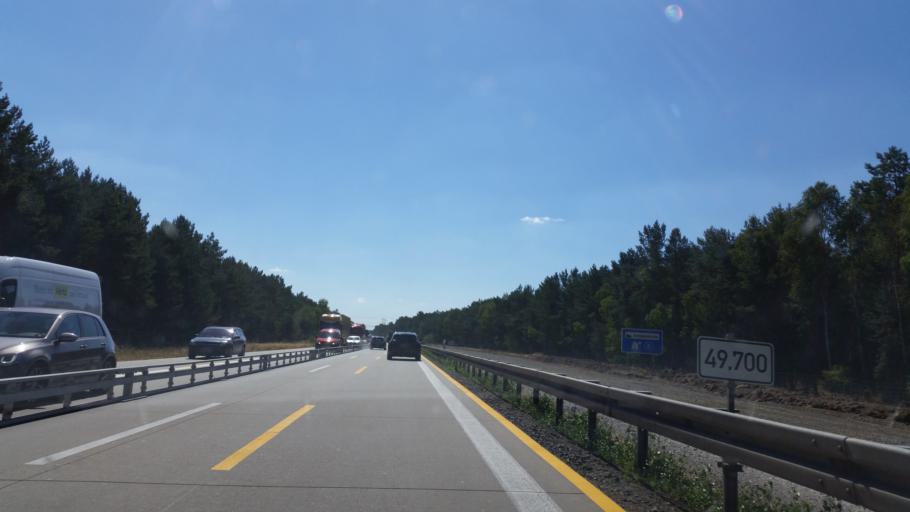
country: DE
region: Brandenburg
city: Kasel-Golzig
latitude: 51.9156
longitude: 13.7881
